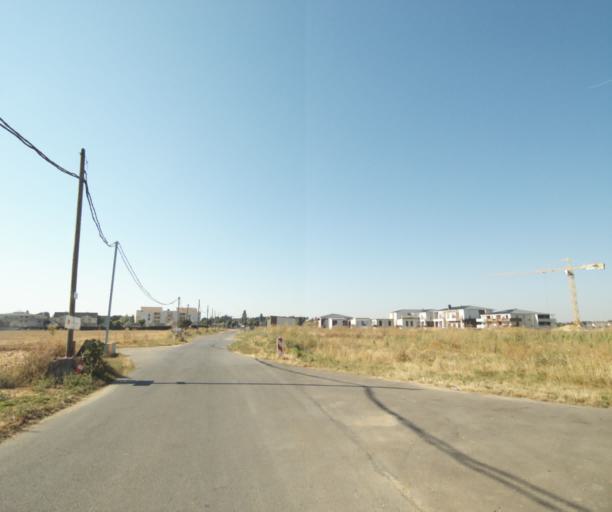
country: FR
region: Ile-de-France
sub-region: Departement de Seine-et-Marne
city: Moissy-Cramayel
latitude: 48.6353
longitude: 2.5865
